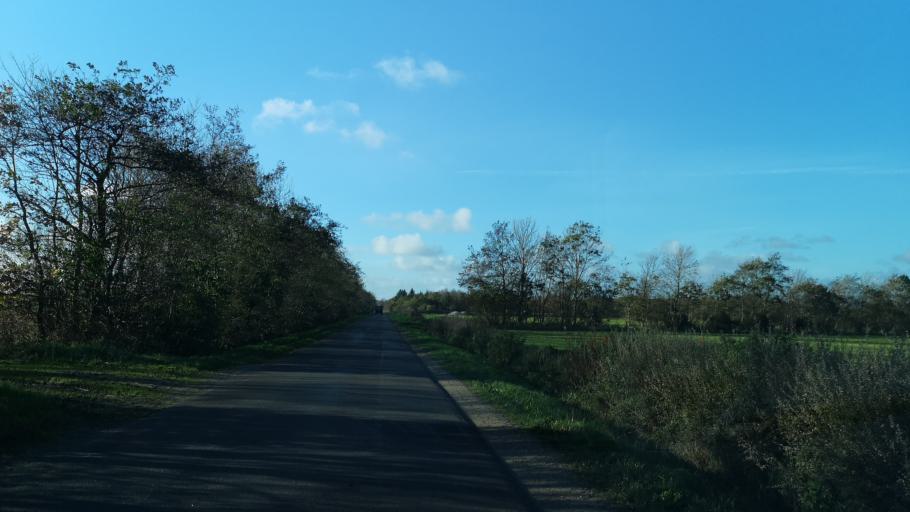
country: DK
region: Central Jutland
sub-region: Ringkobing-Skjern Kommune
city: Tarm
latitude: 55.8257
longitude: 8.3986
